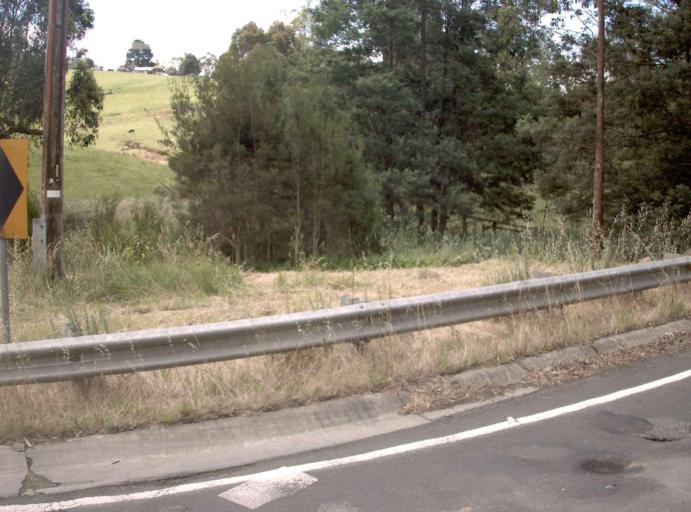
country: AU
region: Victoria
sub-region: Baw Baw
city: Warragul
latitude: -38.0660
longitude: 145.9251
